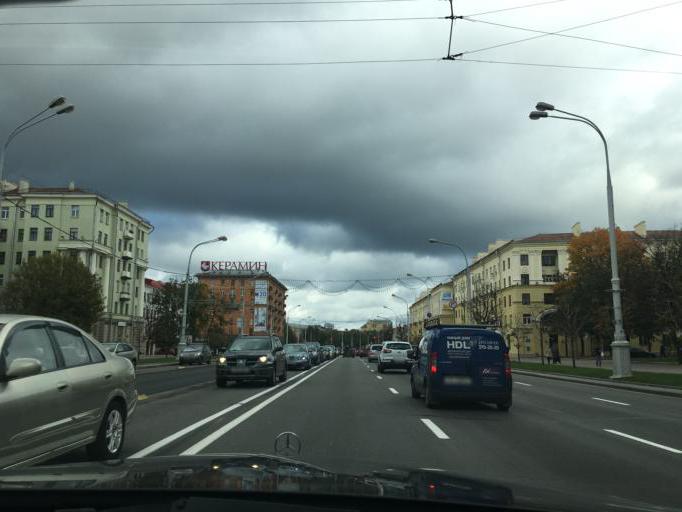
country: BY
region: Minsk
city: Minsk
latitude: 53.9121
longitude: 27.5793
